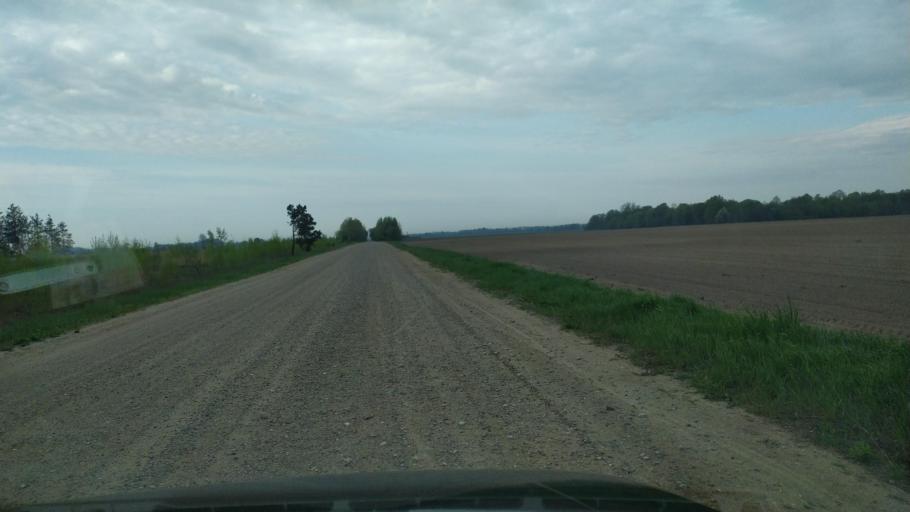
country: BY
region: Brest
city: Zhabinka
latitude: 52.1456
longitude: 24.0940
